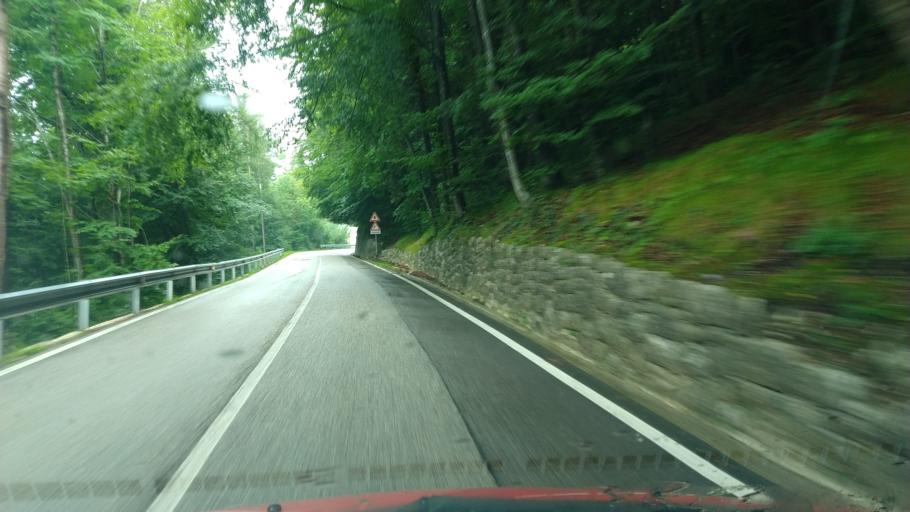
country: IT
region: Veneto
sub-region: Provincia di Vicenza
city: Tonezza del Cimone
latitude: 45.8524
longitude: 11.3525
